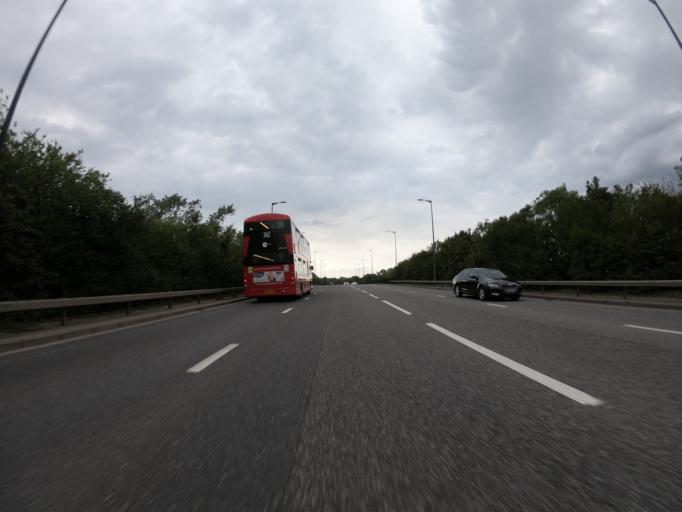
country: GB
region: England
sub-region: Greater London
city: Barking
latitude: 51.5180
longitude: 0.0728
